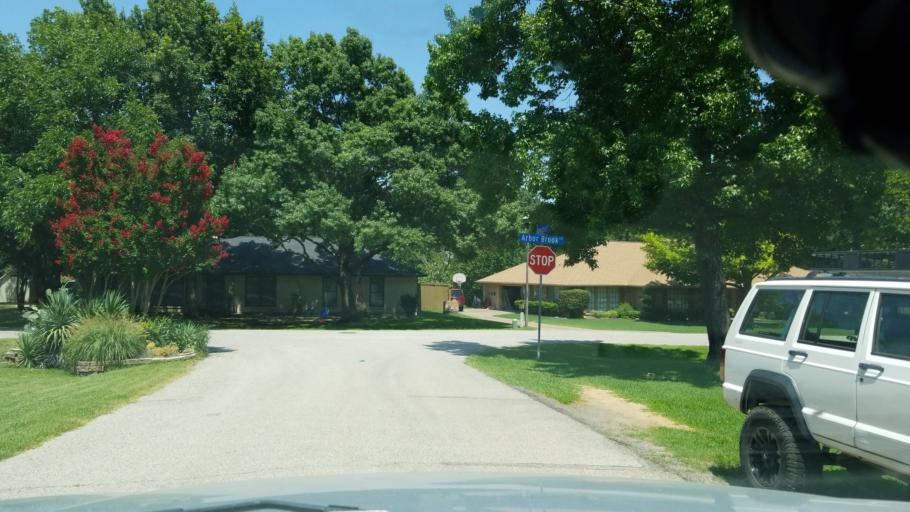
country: US
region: Texas
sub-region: Dallas County
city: Coppell
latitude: 32.9570
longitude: -96.9864
